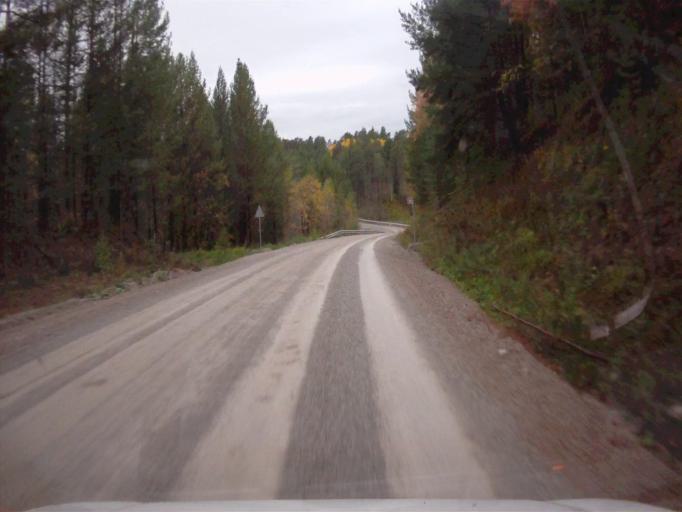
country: RU
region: Chelyabinsk
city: Nyazepetrovsk
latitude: 56.0591
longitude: 59.4532
